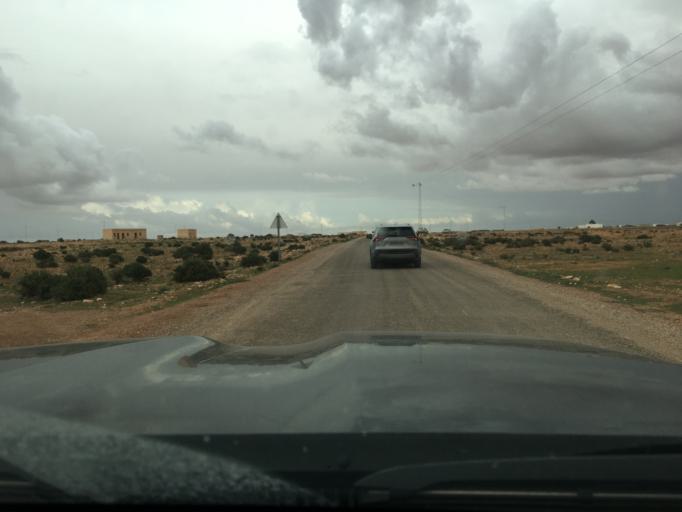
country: TN
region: Madanin
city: Medenine
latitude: 33.2884
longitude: 10.6045
